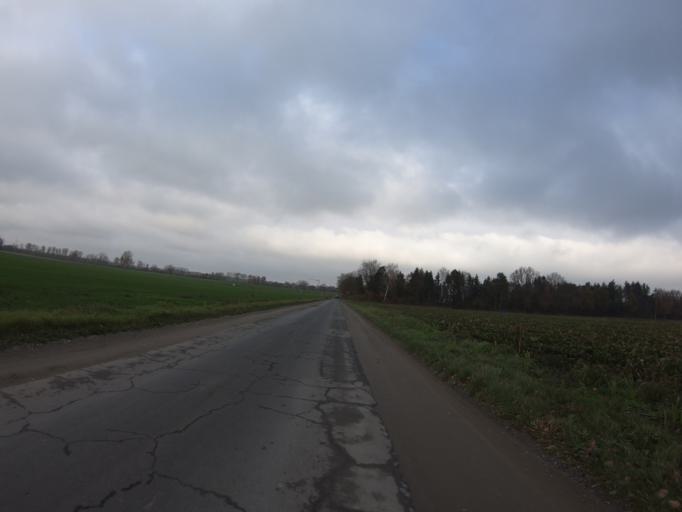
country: DE
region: Lower Saxony
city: Wagenhoff
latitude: 52.5103
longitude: 10.5277
